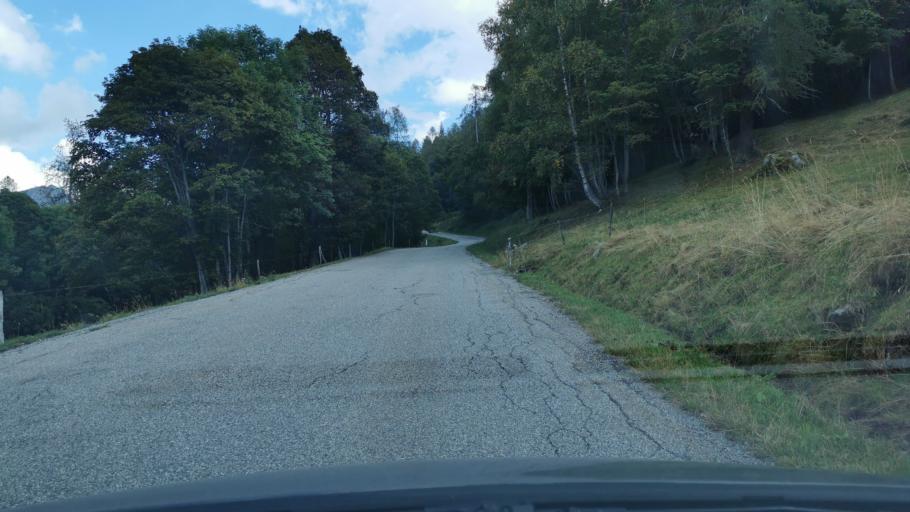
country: IT
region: Piedmont
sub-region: Provincia di Torino
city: Usseglio
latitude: 45.2276
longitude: 7.2111
